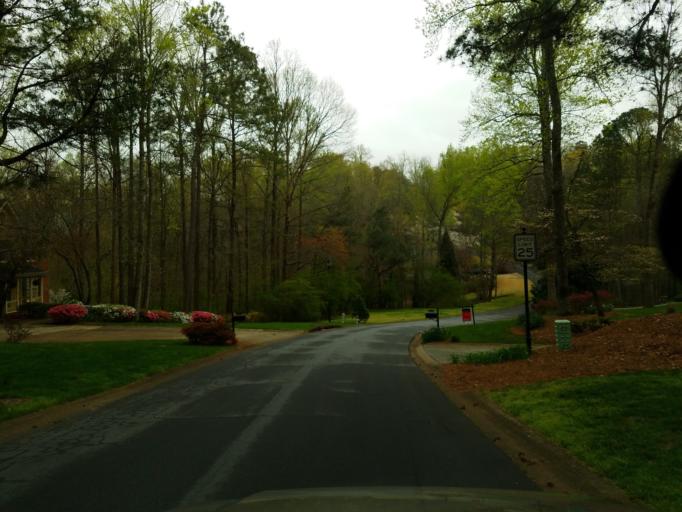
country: US
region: Georgia
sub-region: Fulton County
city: Roswell
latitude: 34.0384
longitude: -84.4165
